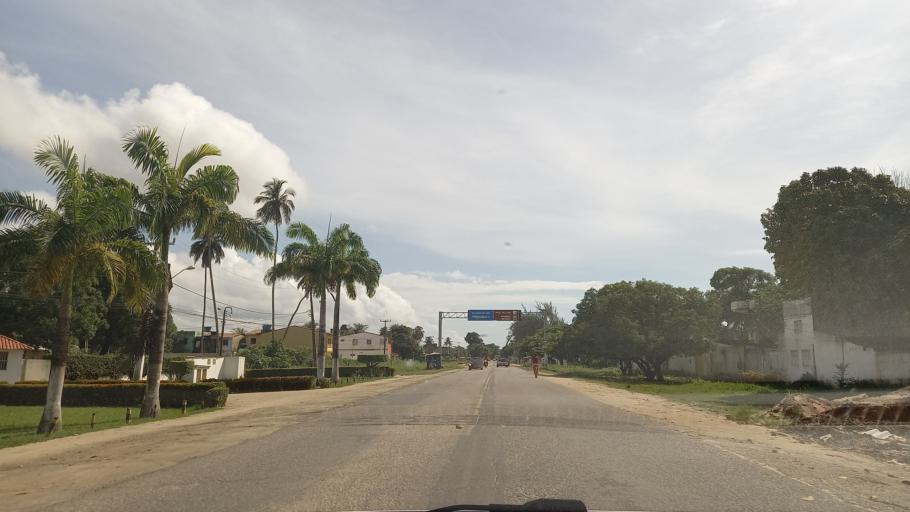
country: BR
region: Pernambuco
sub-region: Sao Jose Da Coroa Grande
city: Sao Jose da Coroa Grande
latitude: -8.9100
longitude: -35.1531
